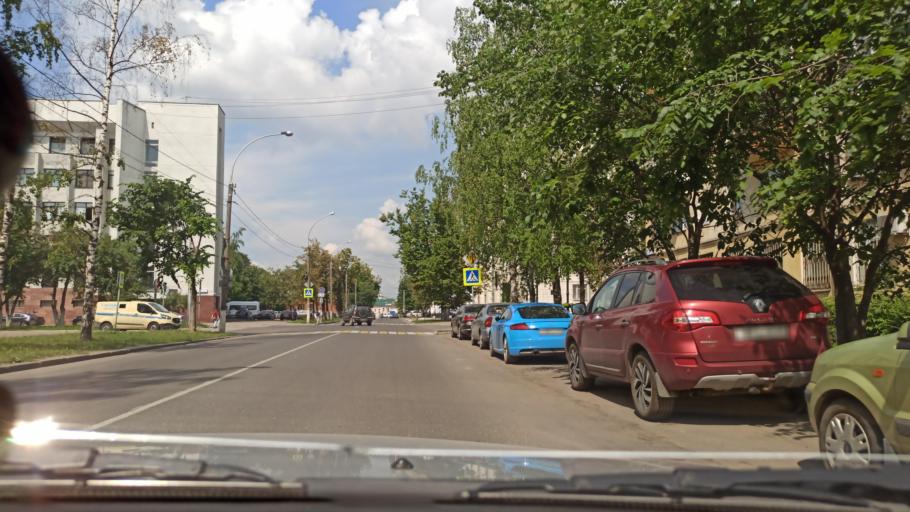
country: RU
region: Vologda
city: Vologda
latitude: 59.2169
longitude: 39.8908
